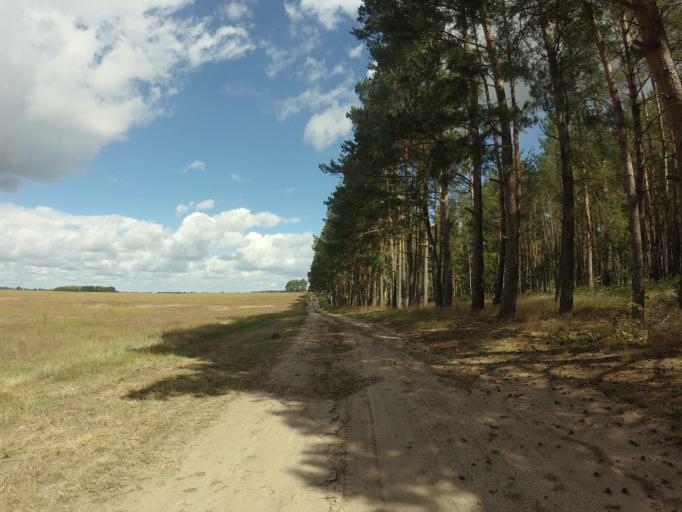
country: PL
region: West Pomeranian Voivodeship
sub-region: Powiat choszczenski
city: Drawno
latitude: 53.2429
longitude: 15.6691
